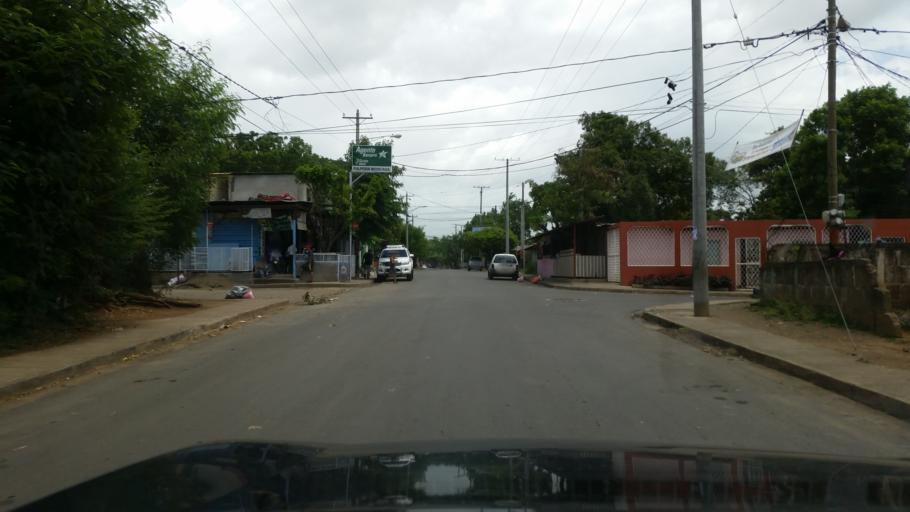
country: NI
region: Managua
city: Managua
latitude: 12.1378
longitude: -86.2135
